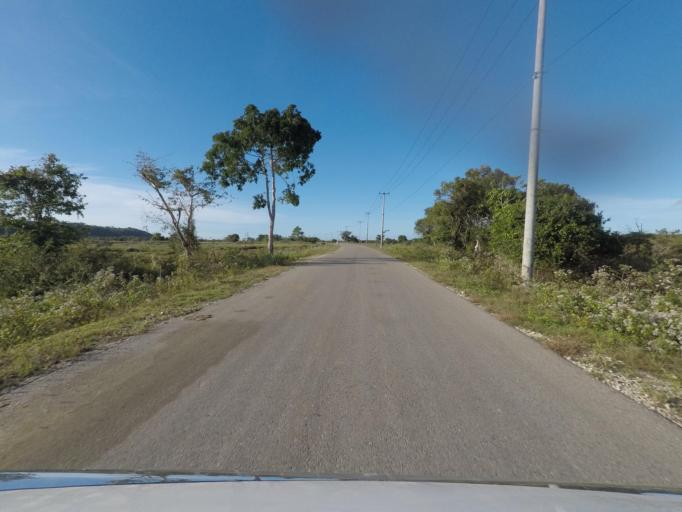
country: TL
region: Lautem
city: Lospalos
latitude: -8.3963
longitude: 127.0078
